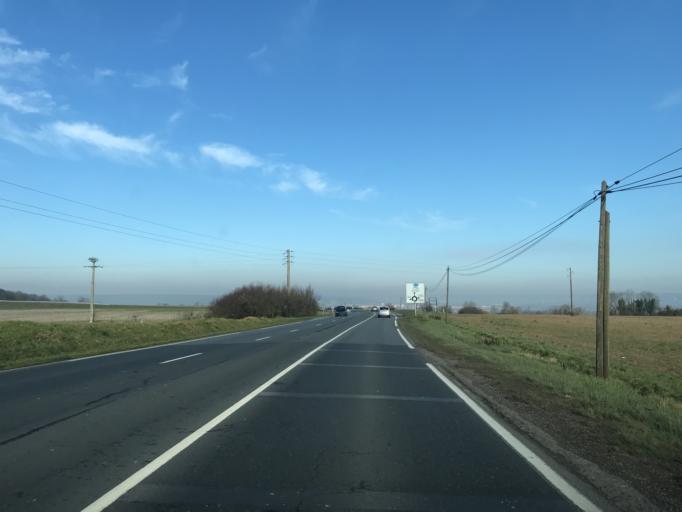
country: FR
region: Haute-Normandie
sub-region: Departement de l'Eure
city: Saint-Pierre-du-Vauvray
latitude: 49.2239
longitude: 1.2128
